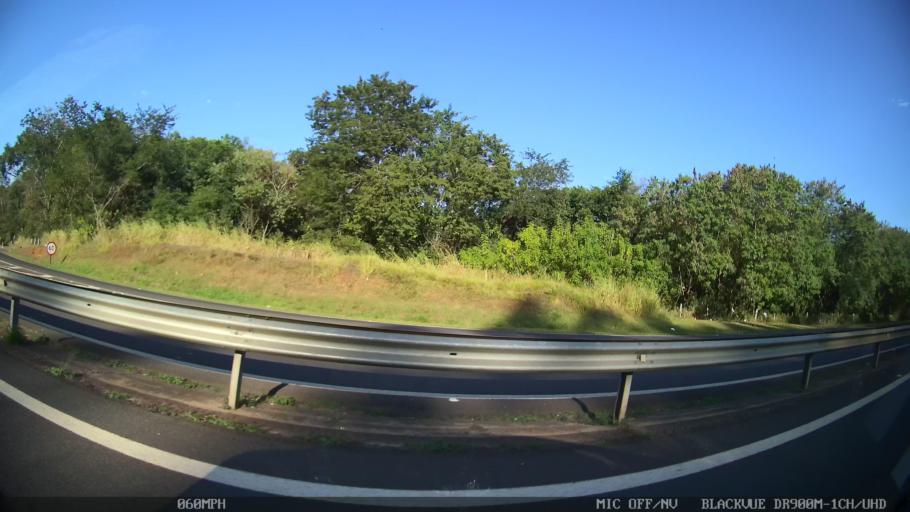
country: BR
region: Sao Paulo
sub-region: Piracicaba
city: Piracicaba
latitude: -22.6964
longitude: -47.6375
